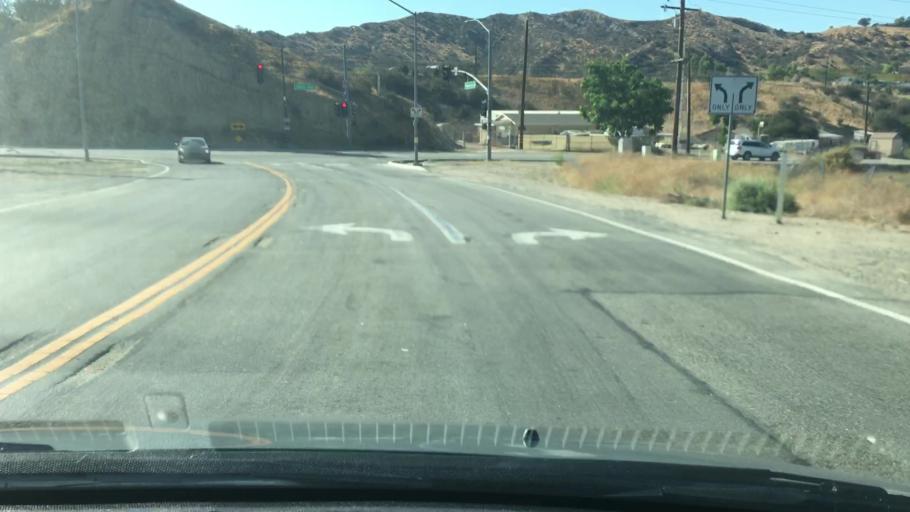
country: US
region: California
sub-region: Los Angeles County
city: Agua Dulce
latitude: 34.4547
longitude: -118.4209
